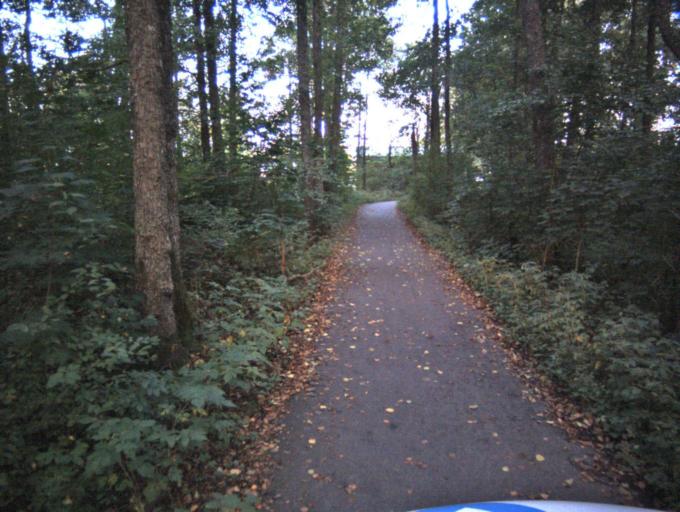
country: SE
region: Vaestra Goetaland
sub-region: Ulricehamns Kommun
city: Ulricehamn
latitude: 57.8012
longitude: 13.4369
